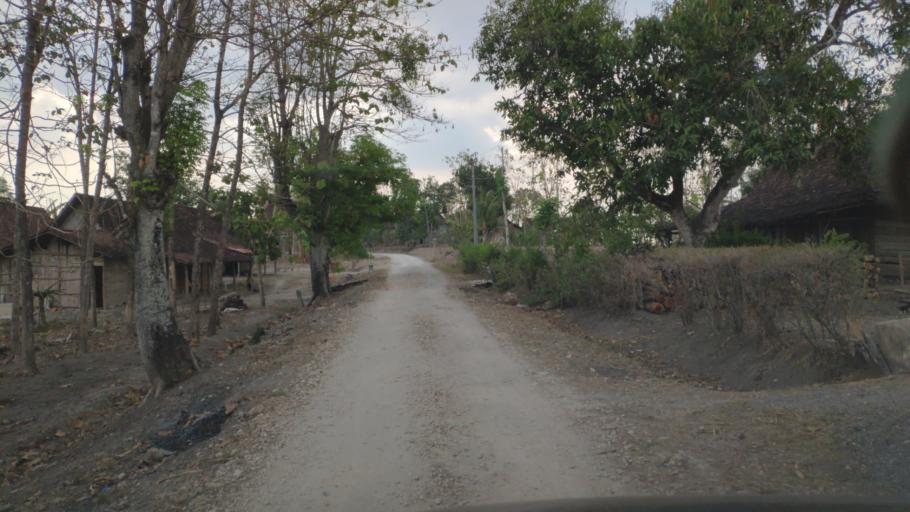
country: ID
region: Central Java
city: Randublatung
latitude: -7.2891
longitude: 111.3098
